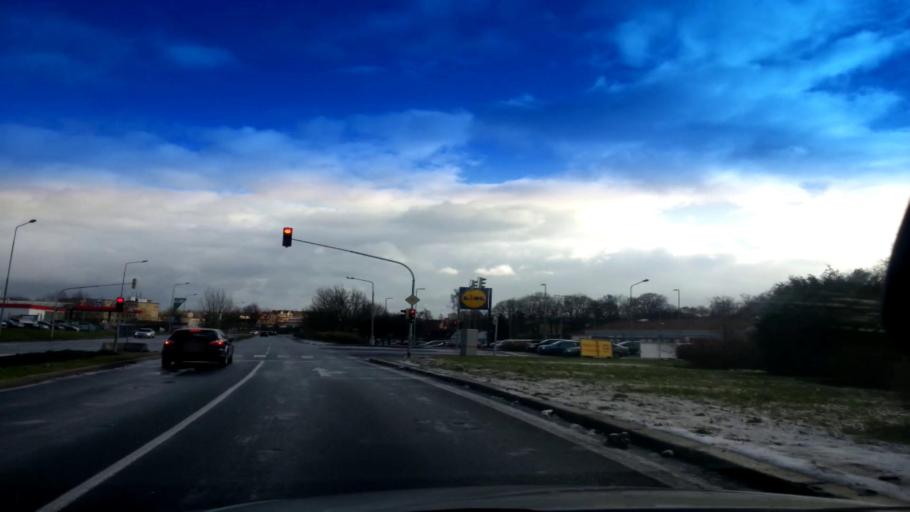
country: CZ
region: Karlovarsky
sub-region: Okres Cheb
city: Cheb
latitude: 50.0843
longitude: 12.3705
